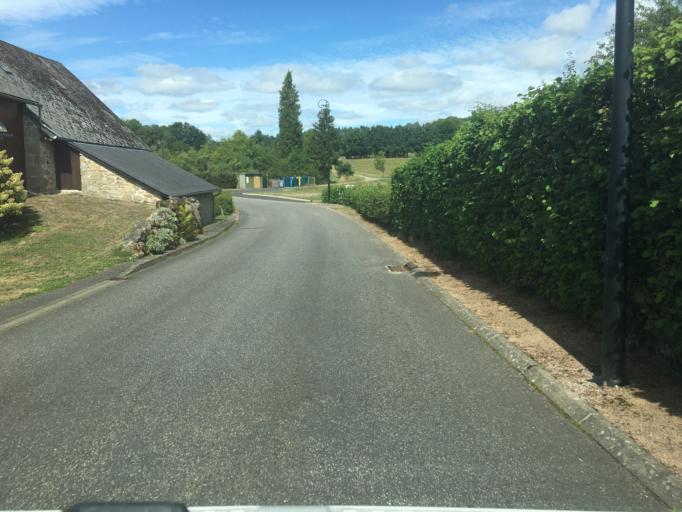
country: FR
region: Auvergne
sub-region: Departement du Cantal
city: Champagnac
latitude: 45.4228
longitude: 2.3802
